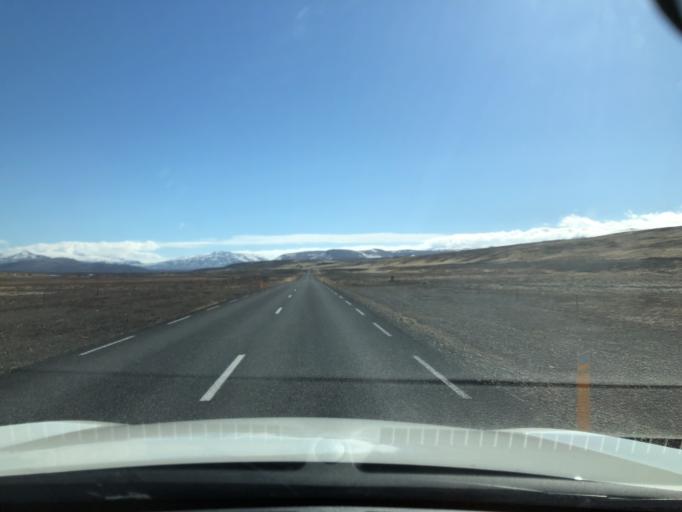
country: IS
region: South
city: Hveragerdi
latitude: 64.7006
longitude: -21.0889
